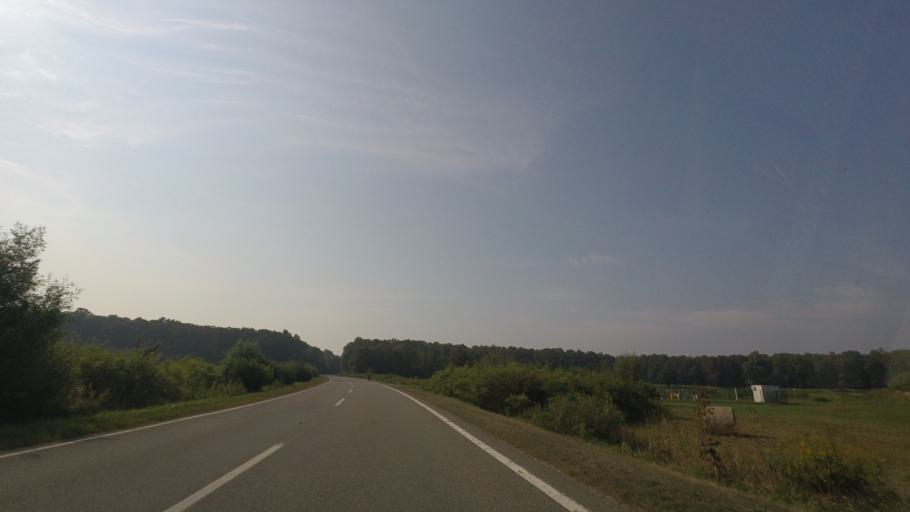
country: HR
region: Sisacko-Moslavacka
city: Novska
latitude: 45.3244
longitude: 16.9484
